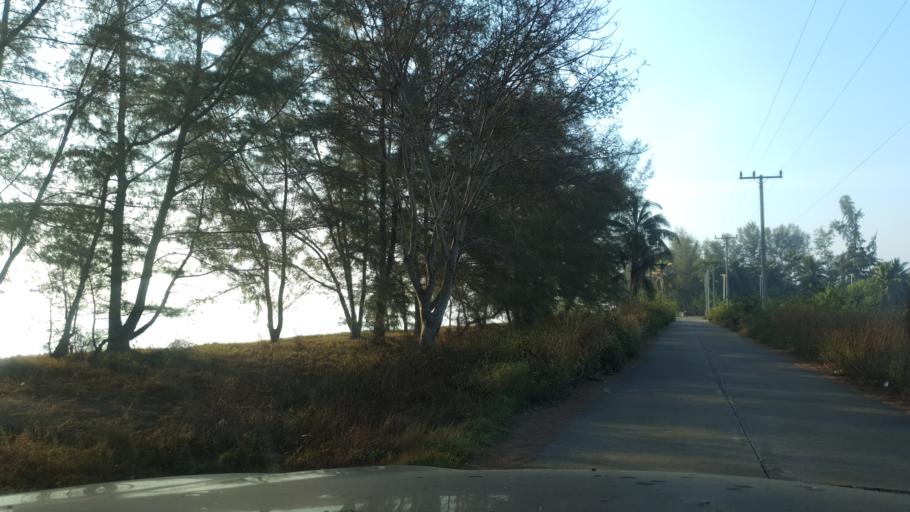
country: TH
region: Prachuap Khiri Khan
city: Bang Saphan
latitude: 11.3065
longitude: 99.5518
